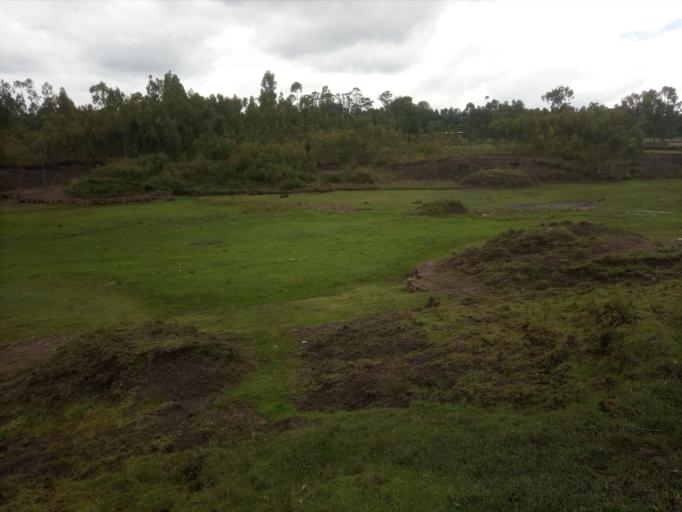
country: ET
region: Southern Nations, Nationalities, and People's Region
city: K'olito
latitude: 7.3401
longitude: 37.9397
